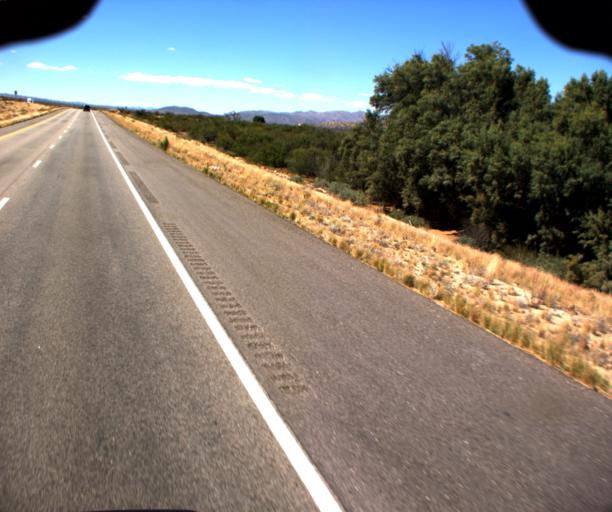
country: US
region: Arizona
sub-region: Yavapai County
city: Bagdad
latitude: 34.8237
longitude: -113.6273
